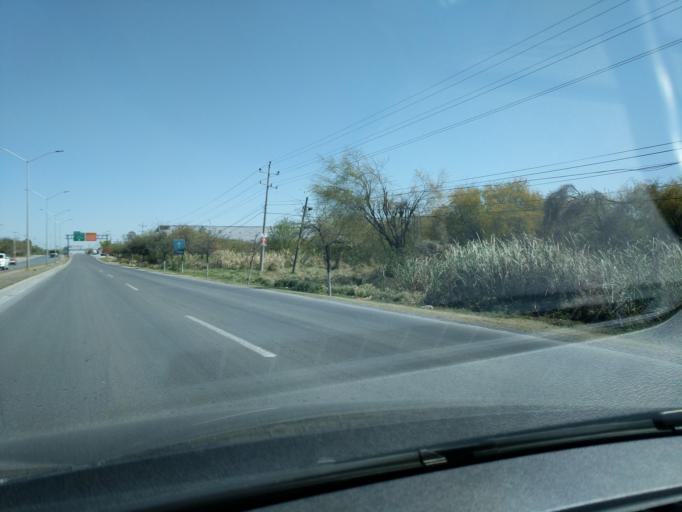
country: MX
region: Nuevo Leon
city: Juarez
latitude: 25.6342
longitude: -100.0801
